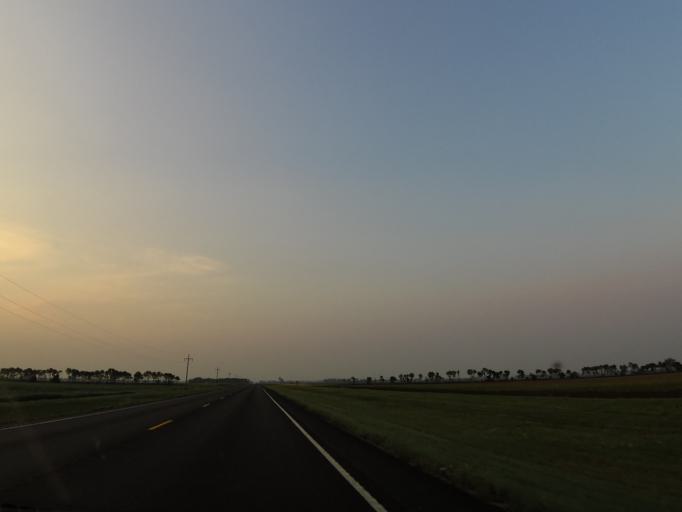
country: US
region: North Dakota
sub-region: Walsh County
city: Park River
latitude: 48.2997
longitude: -97.6218
